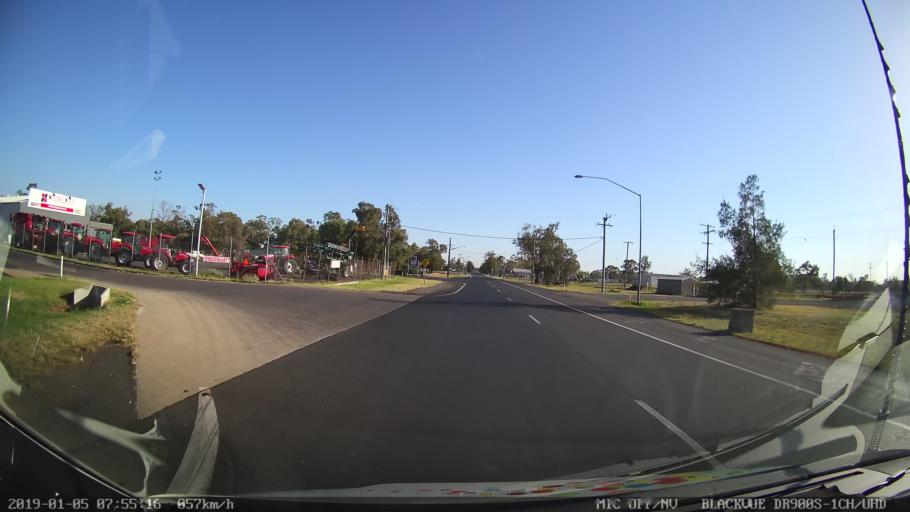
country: AU
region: New South Wales
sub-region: Gilgandra
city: Gilgandra
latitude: -31.7258
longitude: 148.6535
